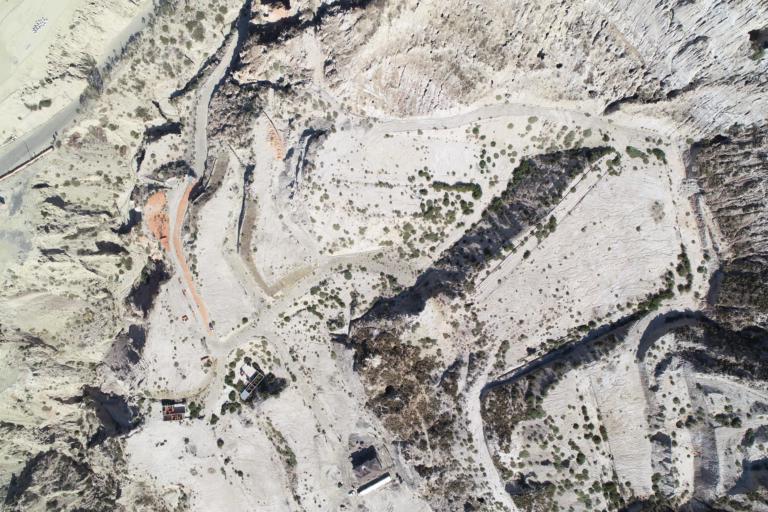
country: BO
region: La Paz
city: La Paz
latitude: -16.5554
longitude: -68.1079
